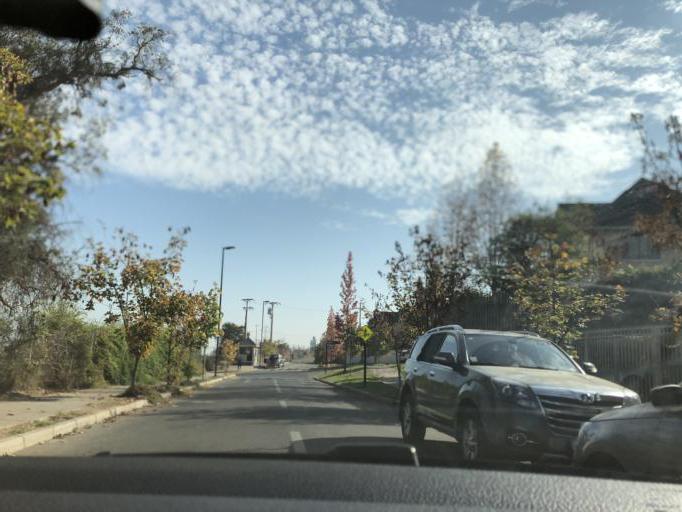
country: CL
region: Santiago Metropolitan
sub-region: Provincia de Cordillera
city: Puente Alto
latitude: -33.5925
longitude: -70.5353
